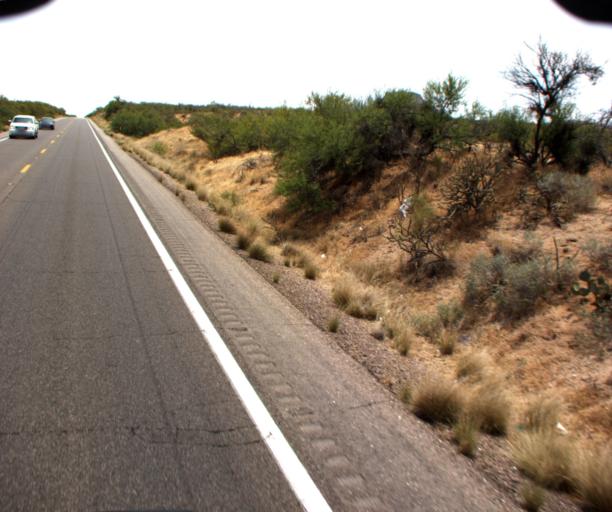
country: US
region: Arizona
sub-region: Gila County
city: Peridot
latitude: 33.3360
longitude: -110.5864
